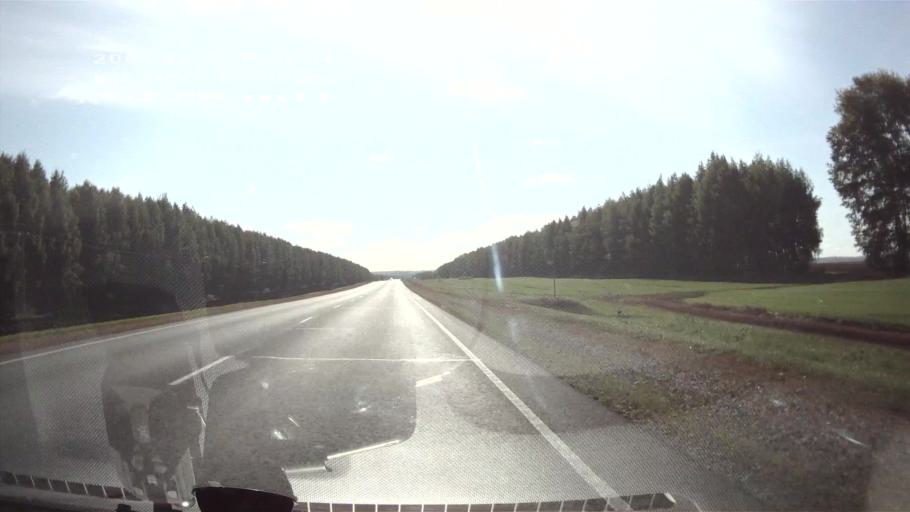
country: RU
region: Ulyanovsk
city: Tsil'na
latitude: 54.5449
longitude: 47.9524
